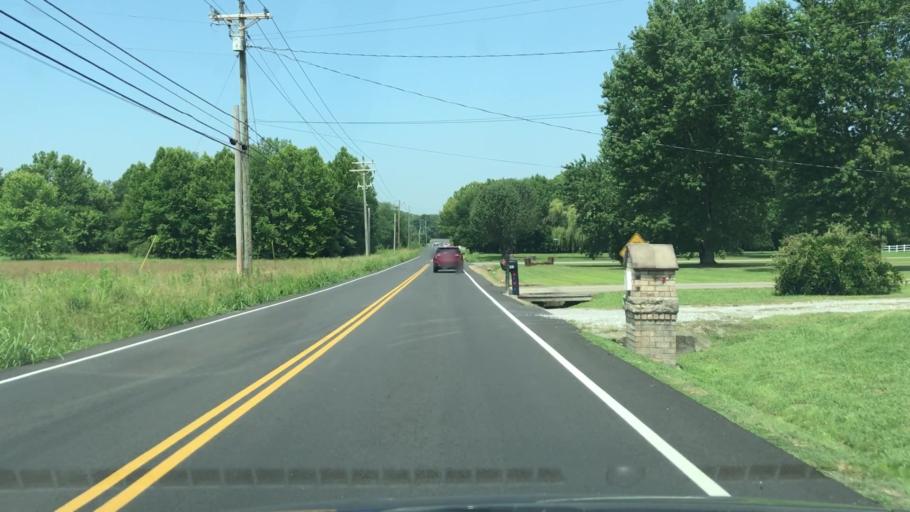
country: US
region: Tennessee
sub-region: Wilson County
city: Rural Hill
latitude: 36.1175
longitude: -86.4879
